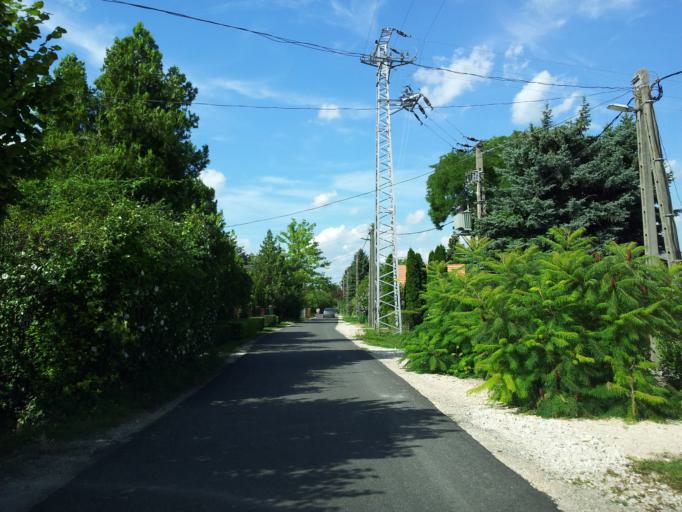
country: HU
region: Pest
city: Szigetcsep
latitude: 47.2585
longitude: 18.9871
